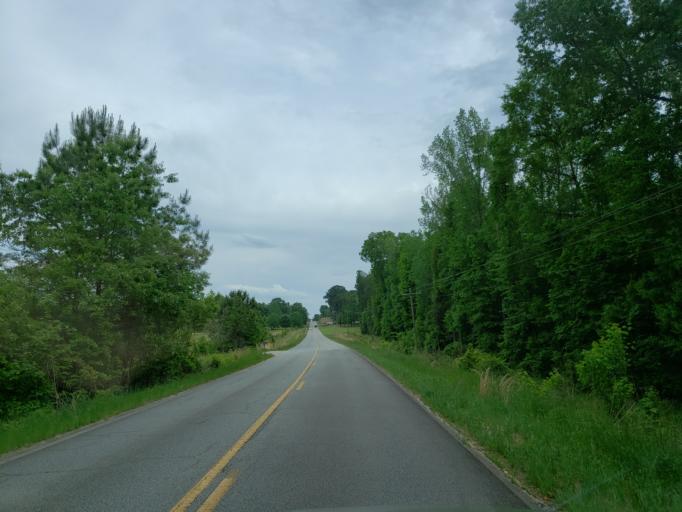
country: US
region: Georgia
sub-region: Bibb County
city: West Point
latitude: 32.8275
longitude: -83.8822
